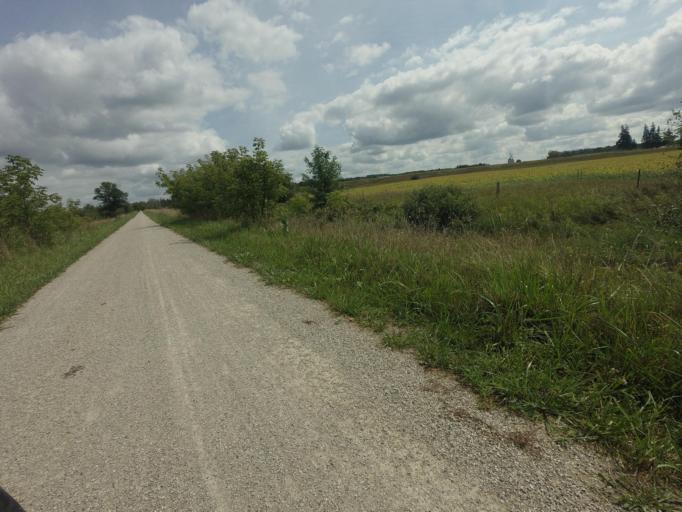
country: CA
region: Ontario
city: North Perth
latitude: 43.5673
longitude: -80.9357
